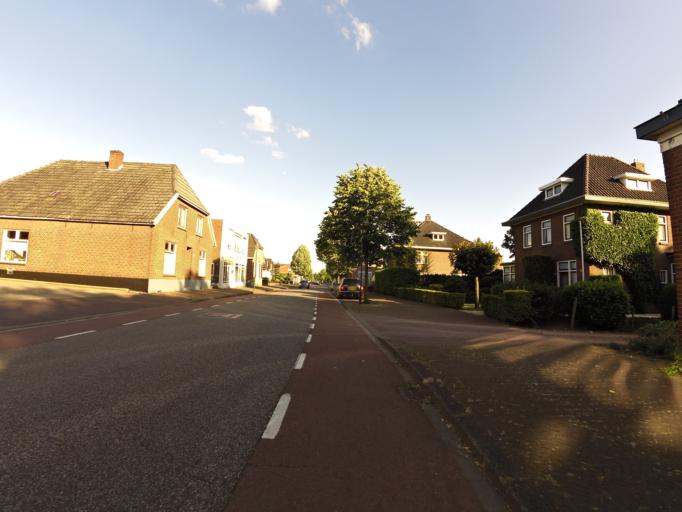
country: NL
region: Gelderland
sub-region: Oude IJsselstreek
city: Gendringen
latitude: 51.9091
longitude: 6.3818
